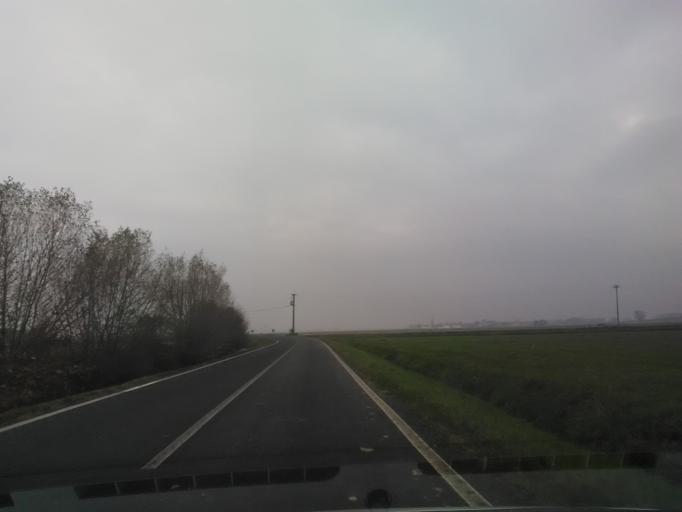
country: IT
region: Piedmont
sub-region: Provincia di Vercelli
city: Salasco
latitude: 45.3157
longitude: 8.2392
